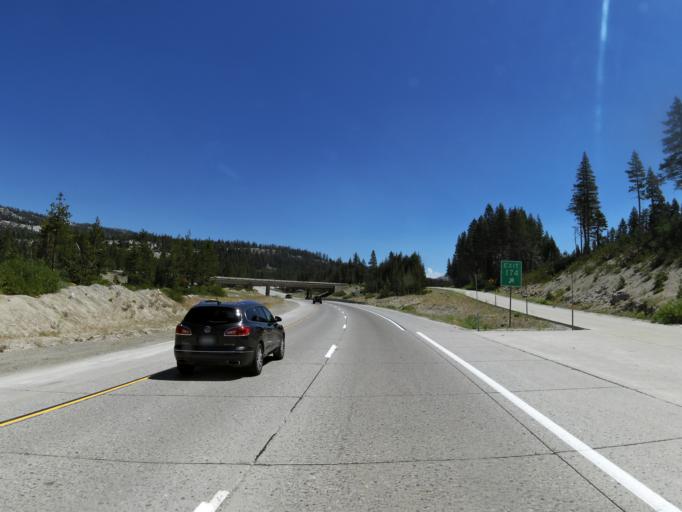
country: US
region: California
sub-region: Nevada County
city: Truckee
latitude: 39.3243
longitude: -120.3946
